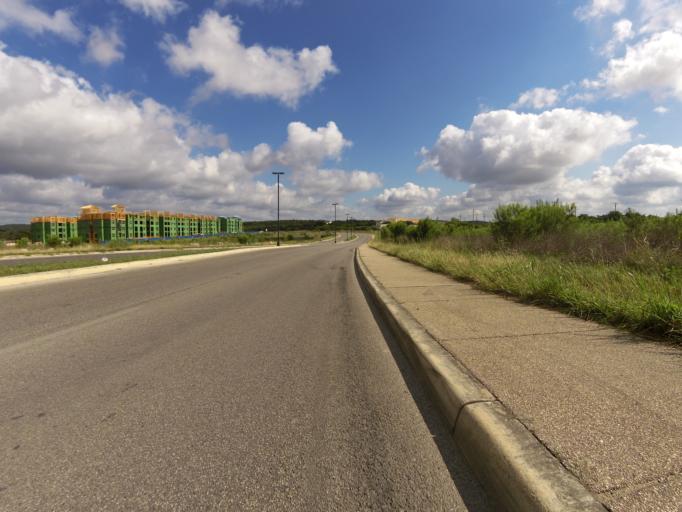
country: US
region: Texas
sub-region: Bexar County
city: Shavano Park
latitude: 29.5926
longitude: -98.5894
